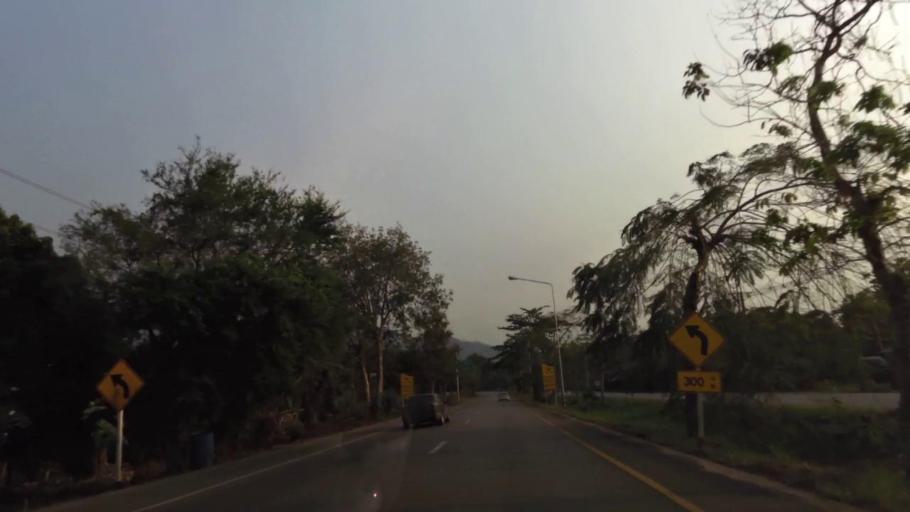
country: TH
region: Chanthaburi
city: Chanthaburi
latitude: 12.5791
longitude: 102.1594
